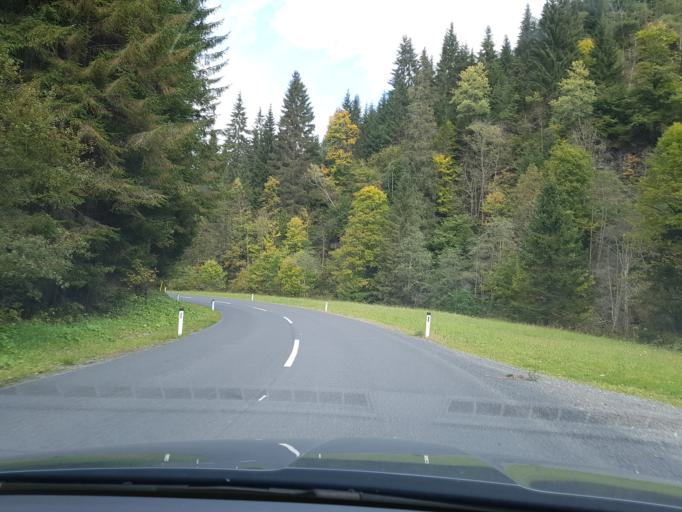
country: AT
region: Styria
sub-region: Politischer Bezirk Murau
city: Stadl an der Mur
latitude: 47.0393
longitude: 13.9058
